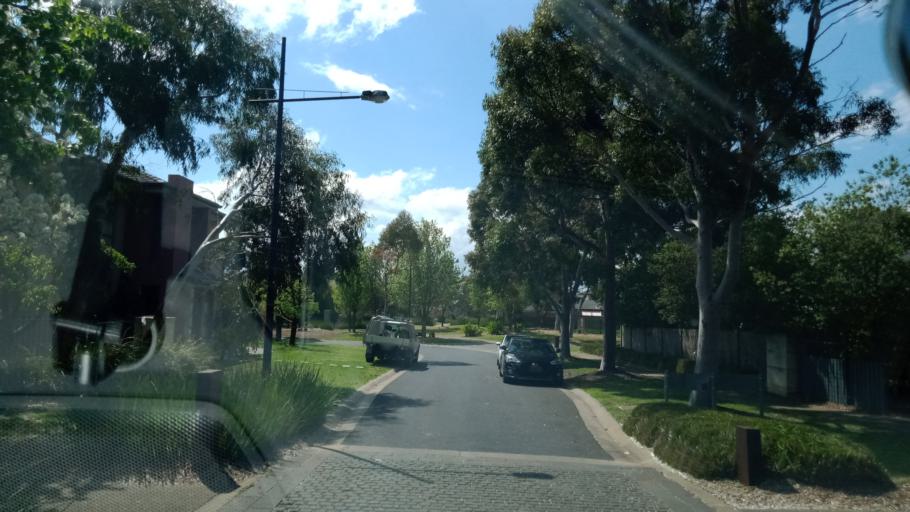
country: AU
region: Victoria
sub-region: Frankston
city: Sandhurst
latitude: -38.0799
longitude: 145.2045
